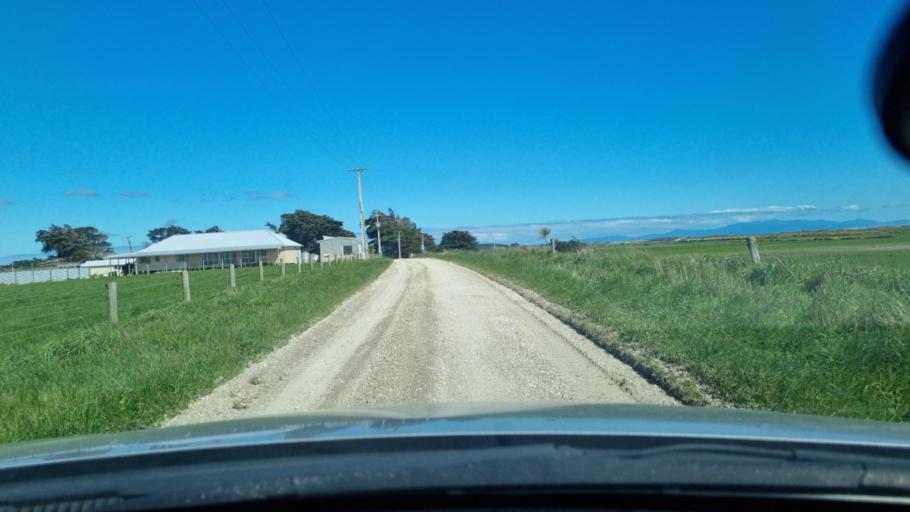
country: NZ
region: Southland
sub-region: Invercargill City
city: Invercargill
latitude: -46.3993
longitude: 168.2563
